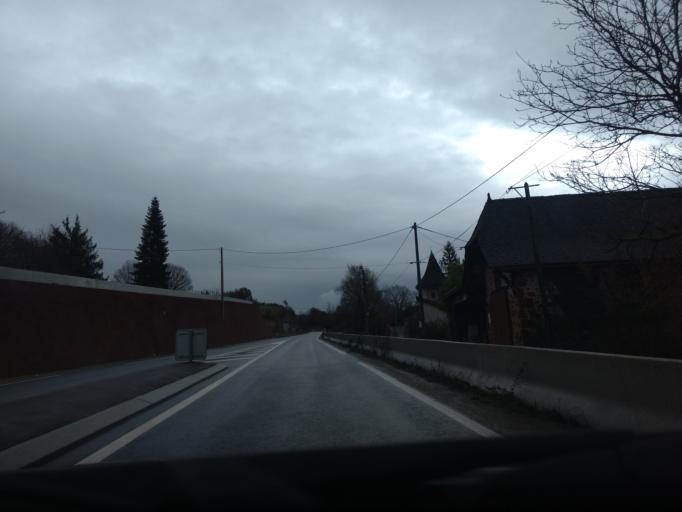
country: FR
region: Midi-Pyrenees
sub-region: Departement de l'Aveyron
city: Firmi
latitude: 44.5131
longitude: 2.3585
